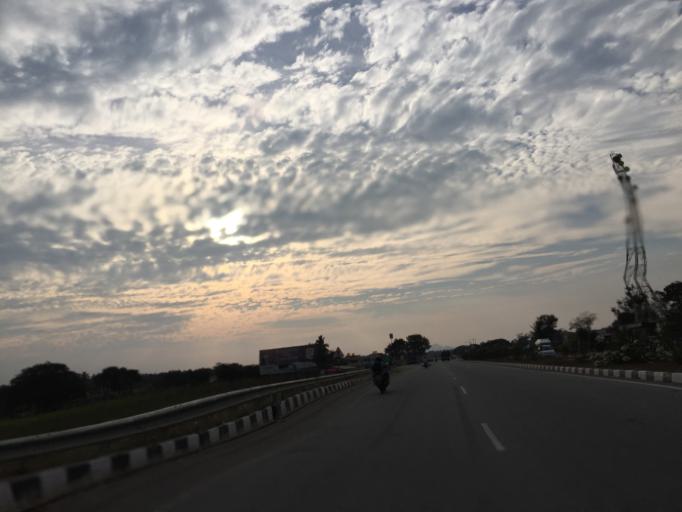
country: IN
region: Karnataka
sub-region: Kolar
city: Kolar
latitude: 13.1469
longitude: 78.2594
